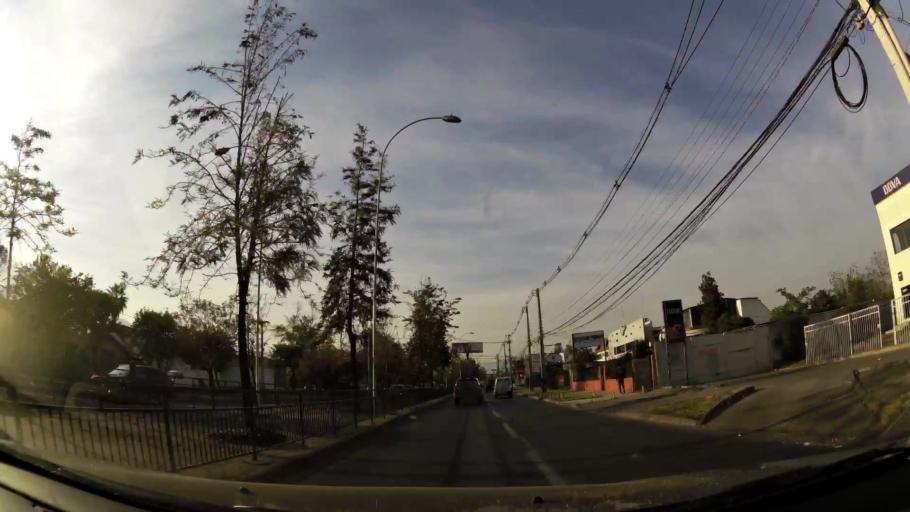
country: CL
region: Santiago Metropolitan
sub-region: Provincia de Cordillera
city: Puente Alto
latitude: -33.5373
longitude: -70.5728
